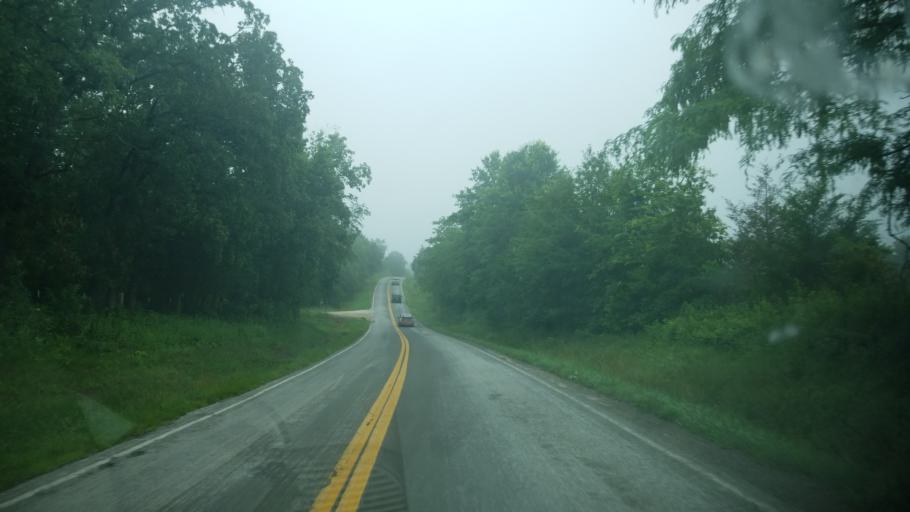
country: US
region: Missouri
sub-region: Audrain County
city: Vandalia
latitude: 39.3175
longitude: -91.3451
